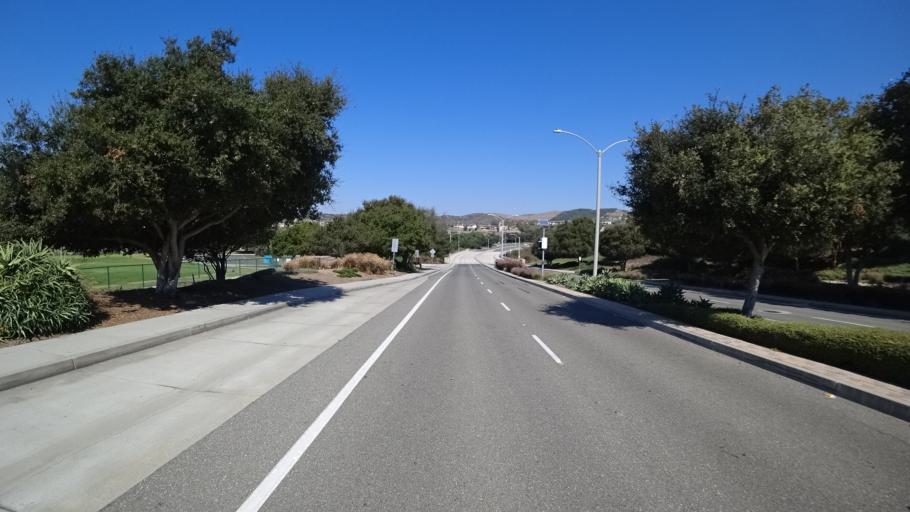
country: US
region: California
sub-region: Orange County
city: San Clemente
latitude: 33.4697
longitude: -117.5971
